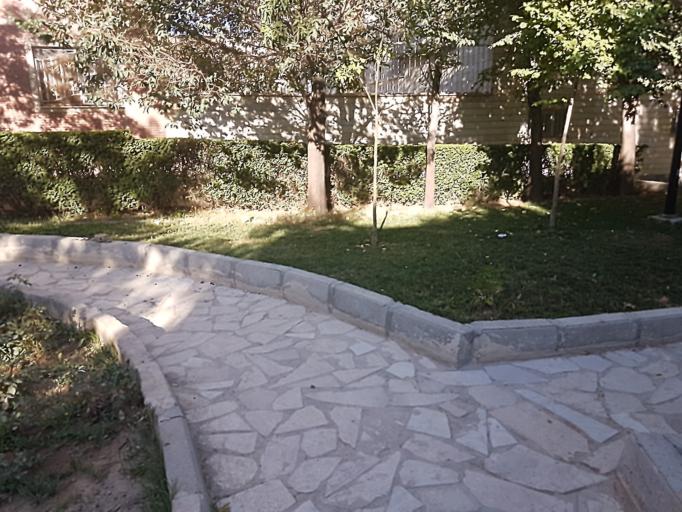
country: IR
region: Markazi
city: Arak
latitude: 34.0661
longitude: 49.6825
